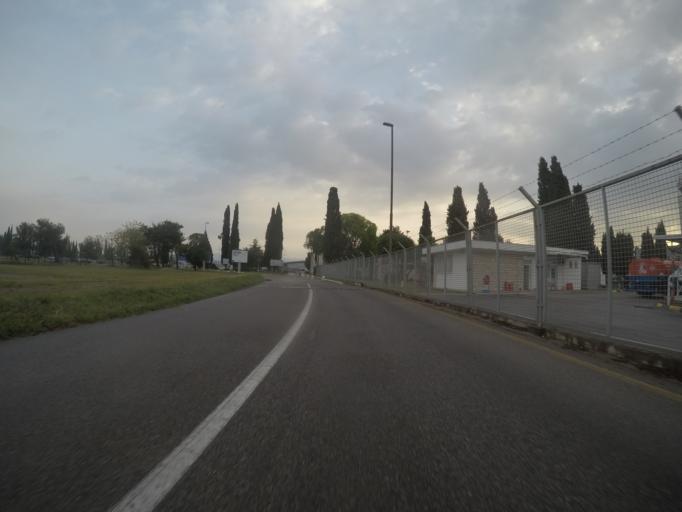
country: ME
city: Golubovci
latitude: 42.3653
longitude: 19.2463
